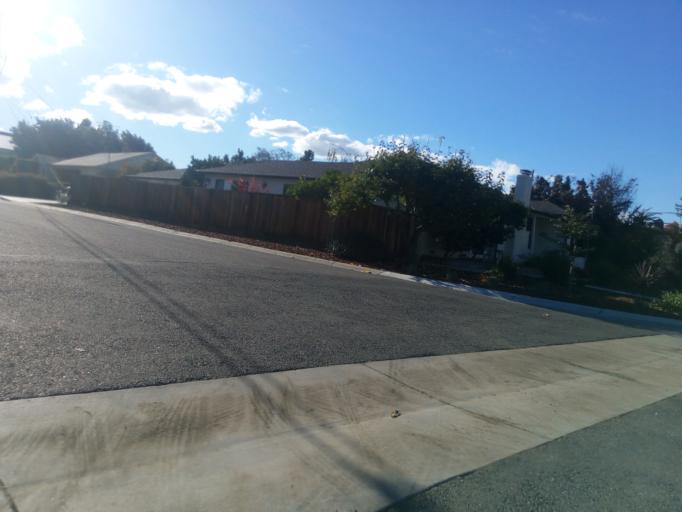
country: US
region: California
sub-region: Santa Clara County
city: Mountain View
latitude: 37.3835
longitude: -122.0841
